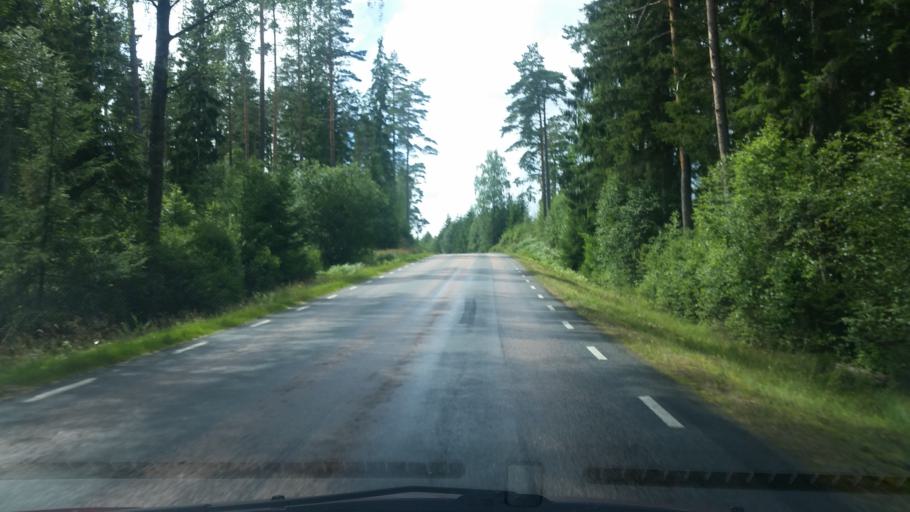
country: SE
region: Joenkoeping
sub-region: Gislaveds Kommun
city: Reftele
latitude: 57.2122
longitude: 13.6173
